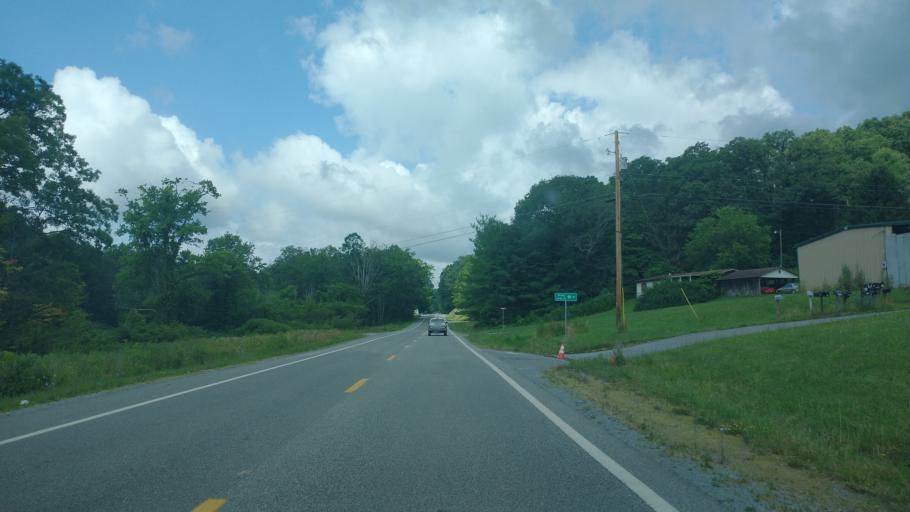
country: US
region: West Virginia
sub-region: Mercer County
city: Bluefield
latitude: 37.3329
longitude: -81.1779
